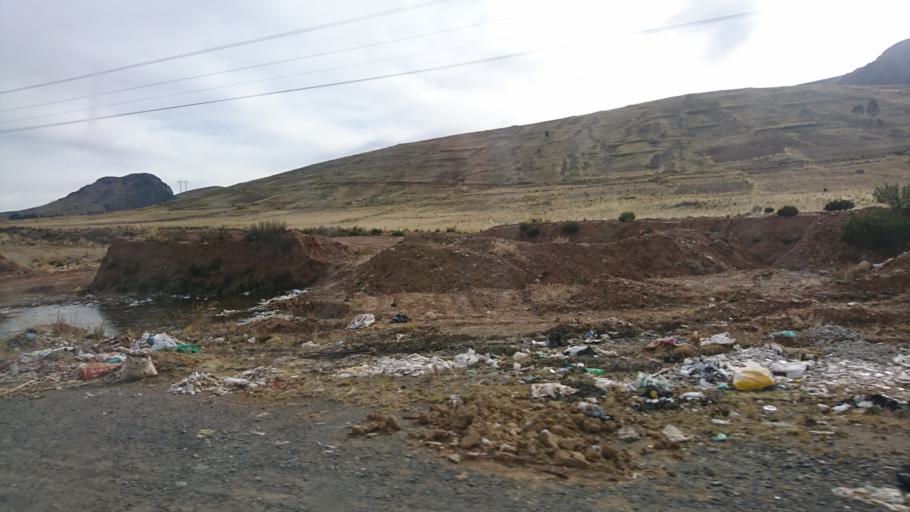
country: BO
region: La Paz
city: Batallas
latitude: -16.4108
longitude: -68.3488
